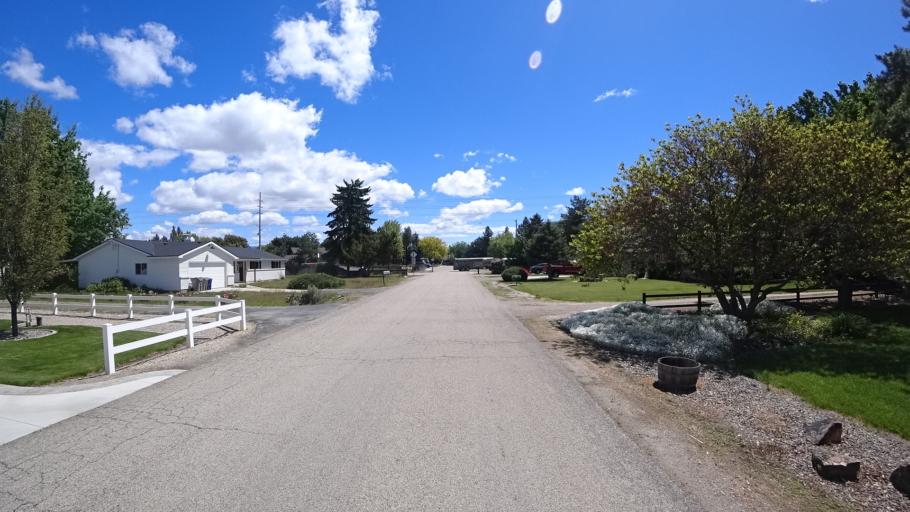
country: US
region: Idaho
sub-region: Ada County
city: Meridian
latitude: 43.6249
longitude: -116.3357
